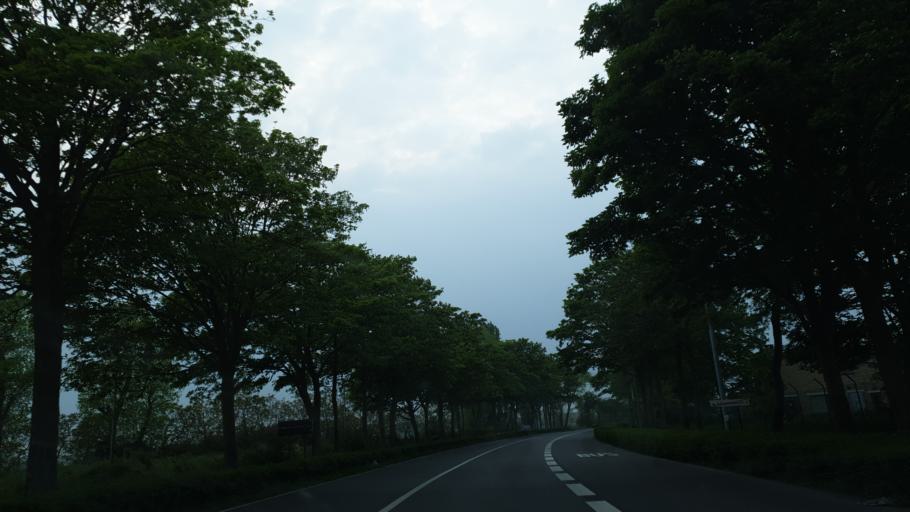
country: BE
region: Flanders
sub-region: Provincie West-Vlaanderen
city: Koksijde
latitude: 51.0859
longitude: 2.6397
